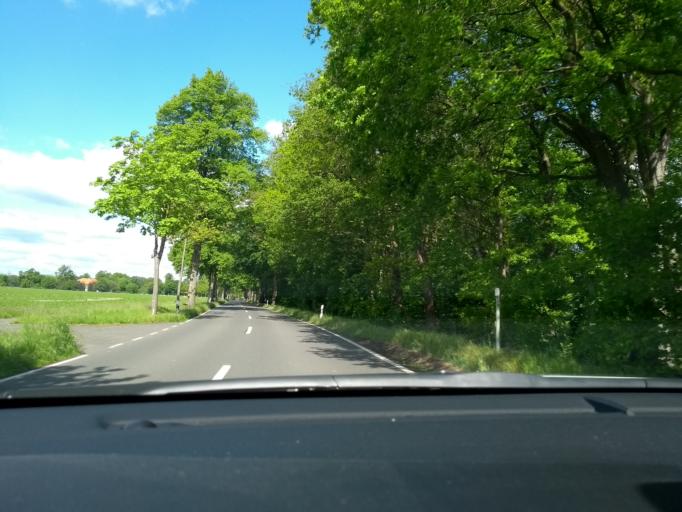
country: DE
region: North Rhine-Westphalia
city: Datteln
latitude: 51.6637
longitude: 7.4002
